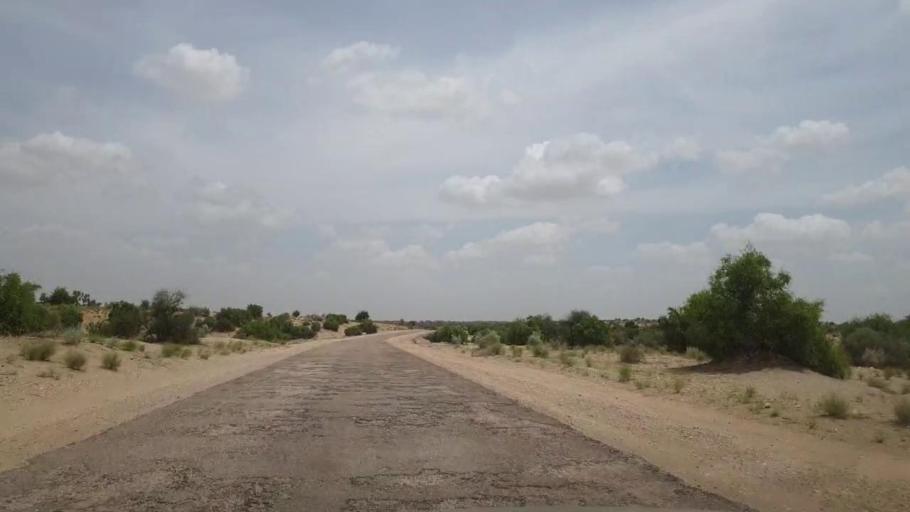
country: PK
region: Sindh
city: Kot Diji
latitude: 27.1881
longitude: 69.1697
